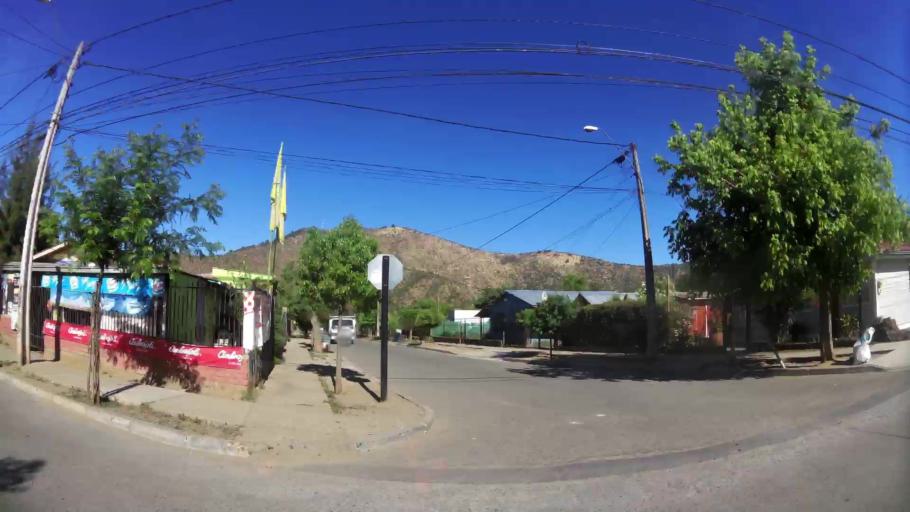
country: CL
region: Santiago Metropolitan
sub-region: Provincia de Chacabuco
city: Lampa
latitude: -33.3971
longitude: -71.1248
